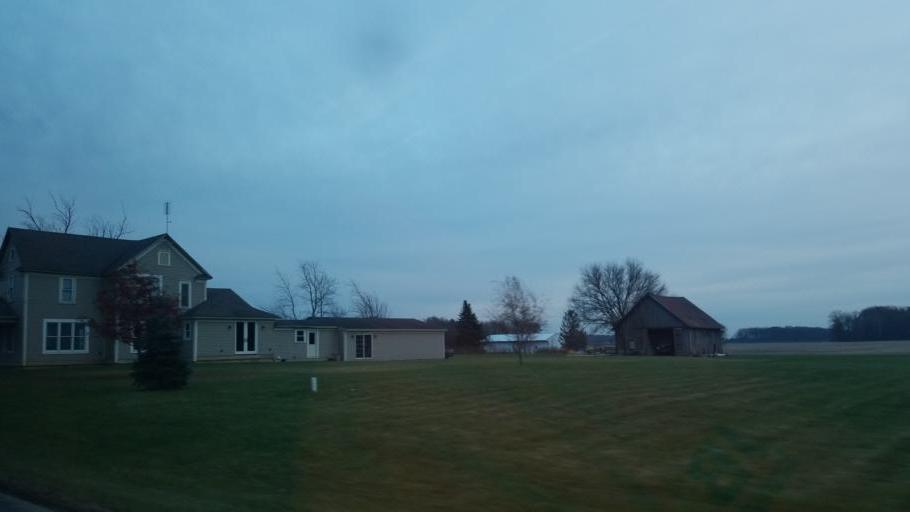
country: US
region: Indiana
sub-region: Adams County
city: Decatur
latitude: 40.7885
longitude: -84.9464
